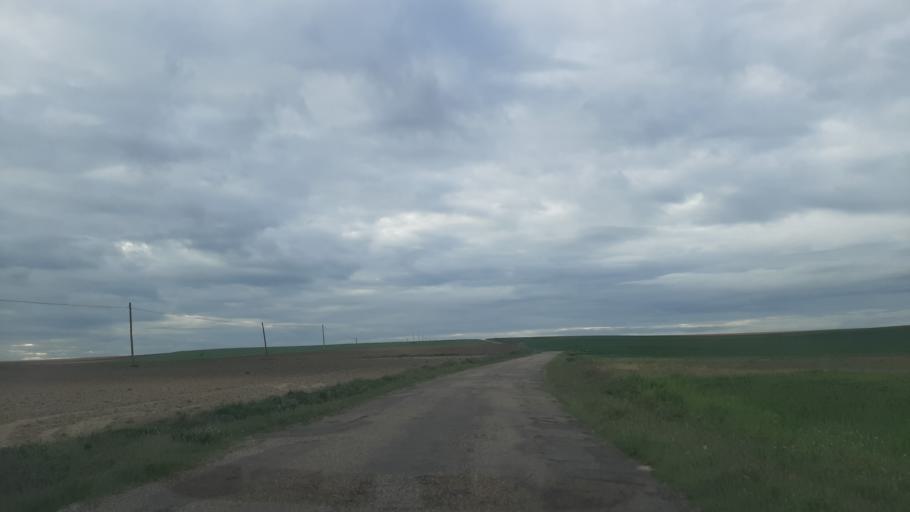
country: ES
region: Castille and Leon
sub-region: Provincia de Salamanca
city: Villaflores
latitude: 41.0728
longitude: -5.2116
